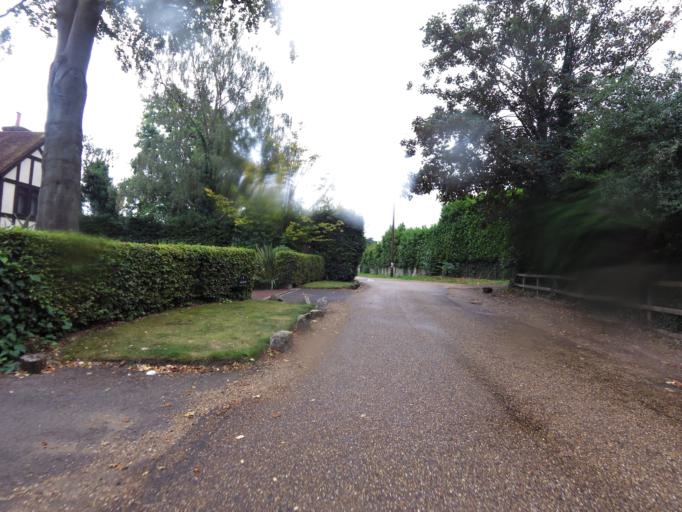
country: GB
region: England
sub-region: Hertfordshire
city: Radlett
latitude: 51.6872
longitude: -0.3238
